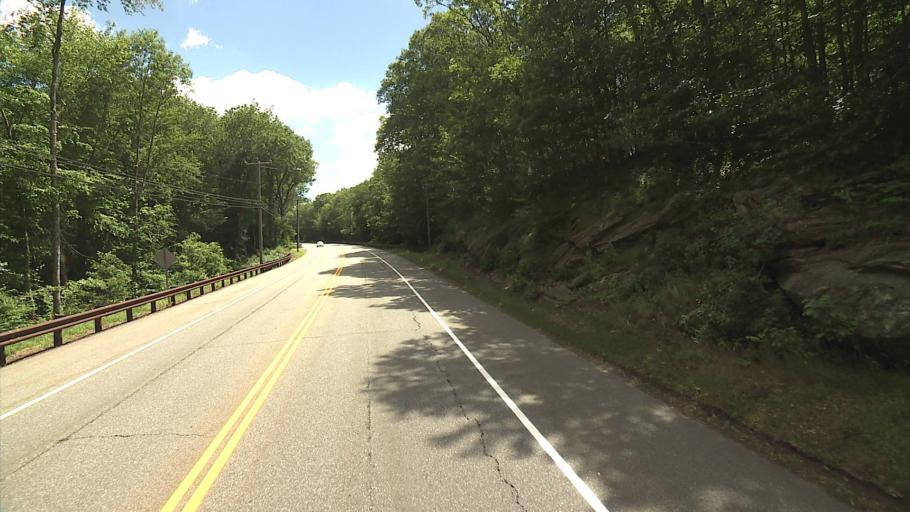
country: US
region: Connecticut
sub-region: New London County
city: Poquonock Bridge
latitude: 41.3842
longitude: -72.0144
